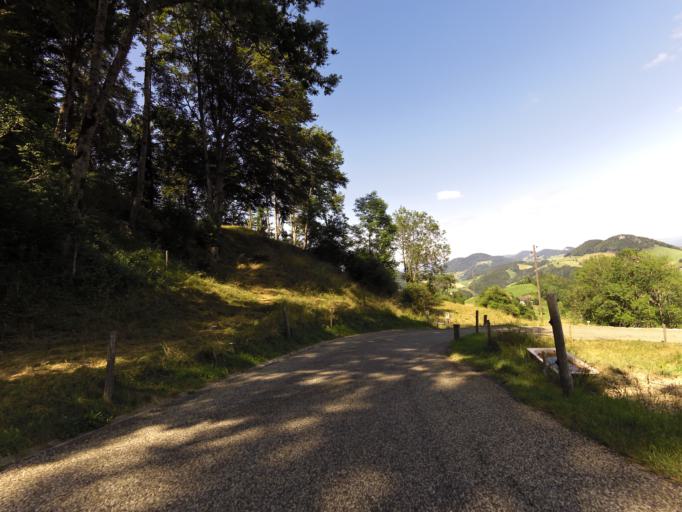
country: CH
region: Basel-Landschaft
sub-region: Bezirk Waldenburg
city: Langenbruck
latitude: 47.3669
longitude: 7.8031
